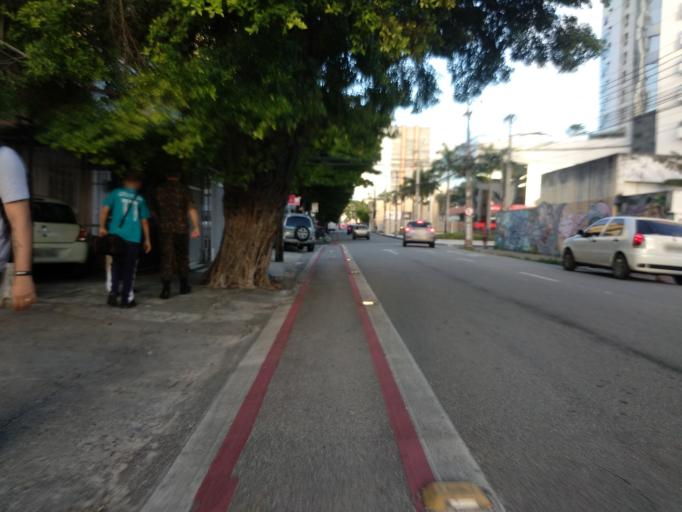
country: BR
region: Ceara
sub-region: Fortaleza
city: Fortaleza
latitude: -3.7304
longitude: -38.5163
